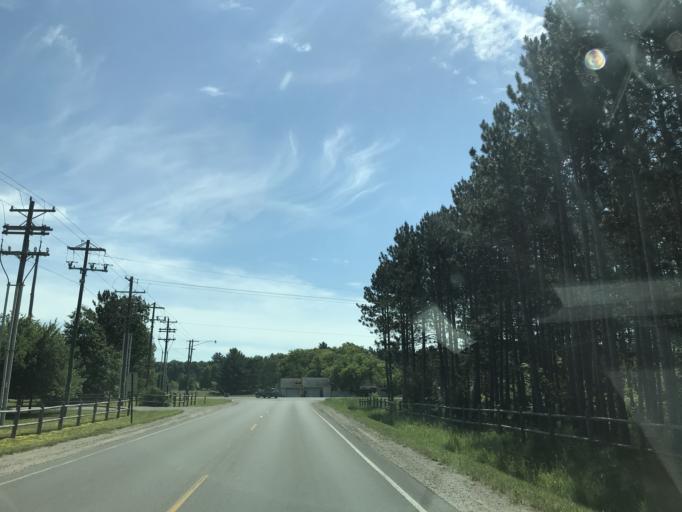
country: US
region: Michigan
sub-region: Grand Traverse County
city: Traverse City
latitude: 44.6541
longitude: -85.6978
